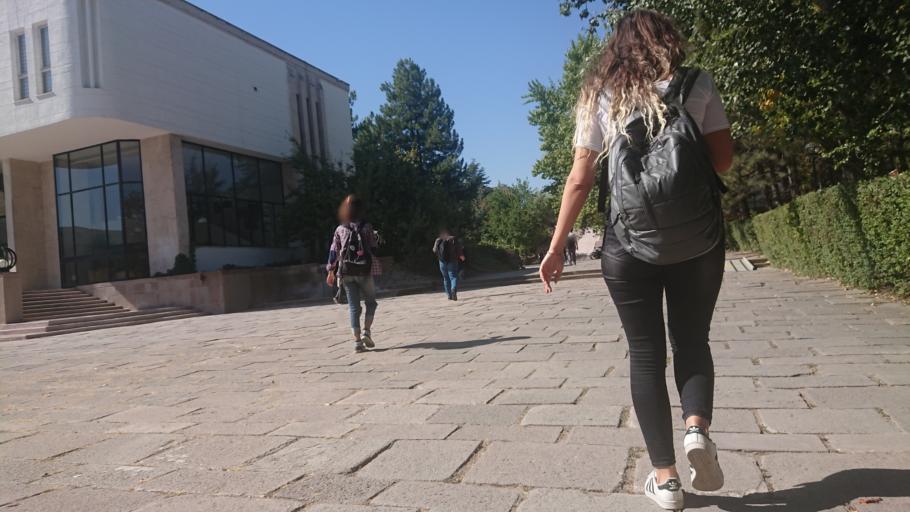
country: TR
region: Ankara
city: Ankara
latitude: 39.8952
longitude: 32.7842
